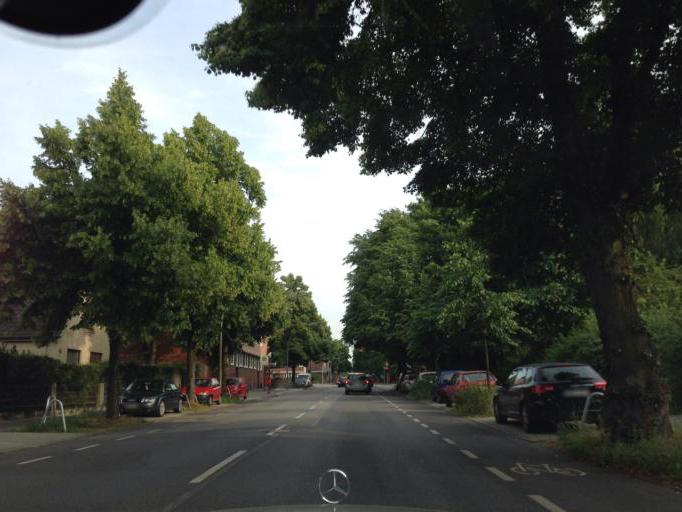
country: DE
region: Hamburg
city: Marienthal
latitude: 53.5860
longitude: 10.0778
